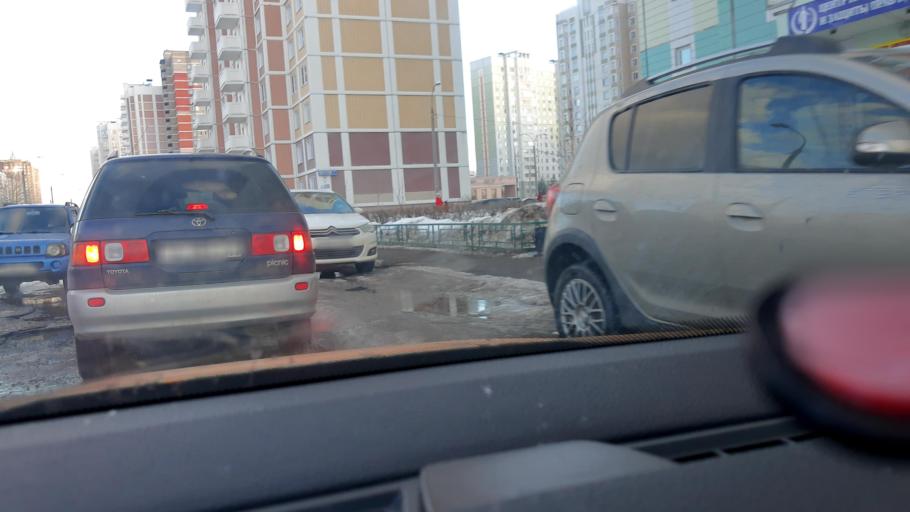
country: RU
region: Moskovskaya
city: Dubrovitsy
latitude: 55.4193
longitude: 37.4773
